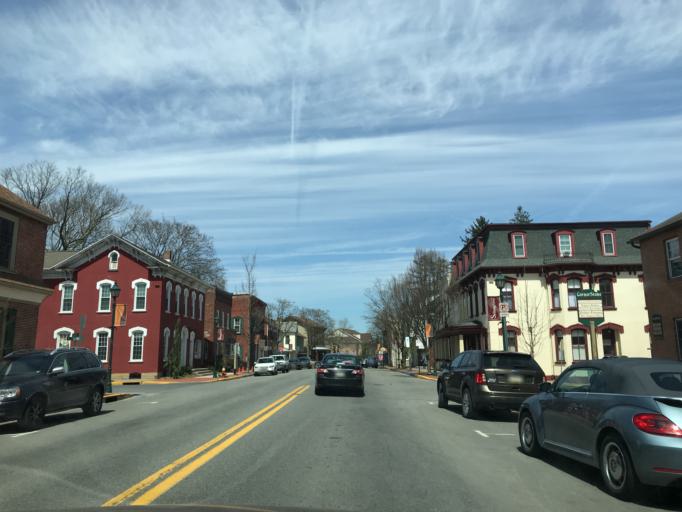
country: US
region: Pennsylvania
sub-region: Snyder County
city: Selinsgrove
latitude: 40.8000
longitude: -76.8618
